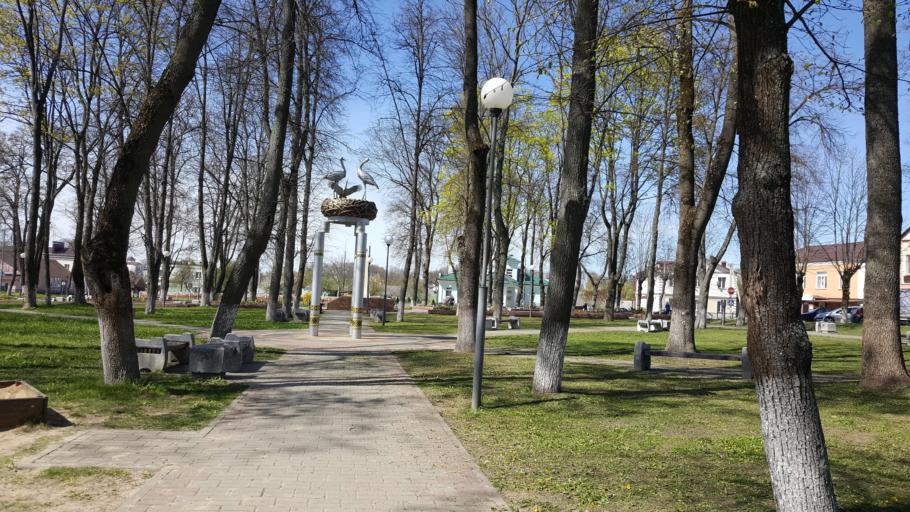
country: BY
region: Brest
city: Vysokaye
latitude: 52.3673
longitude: 23.3770
